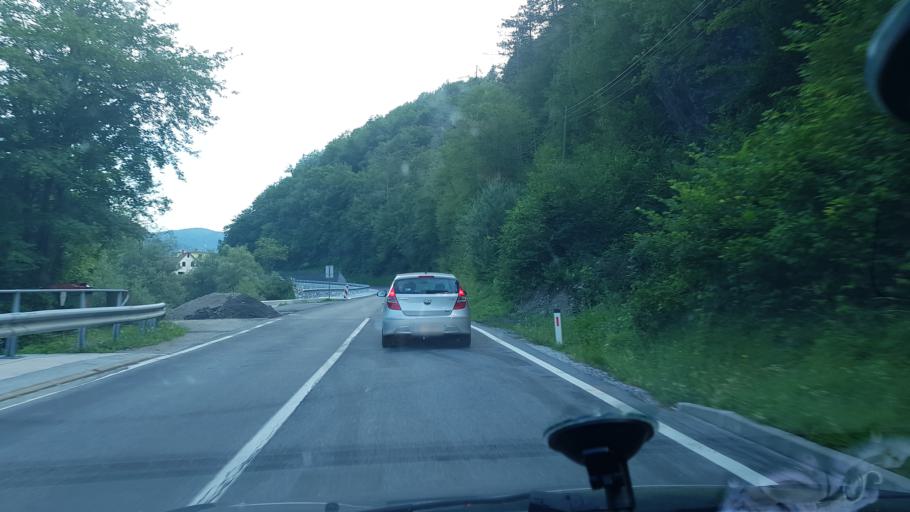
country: SI
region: Idrija
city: Idrija
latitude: 46.0155
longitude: 14.0273
